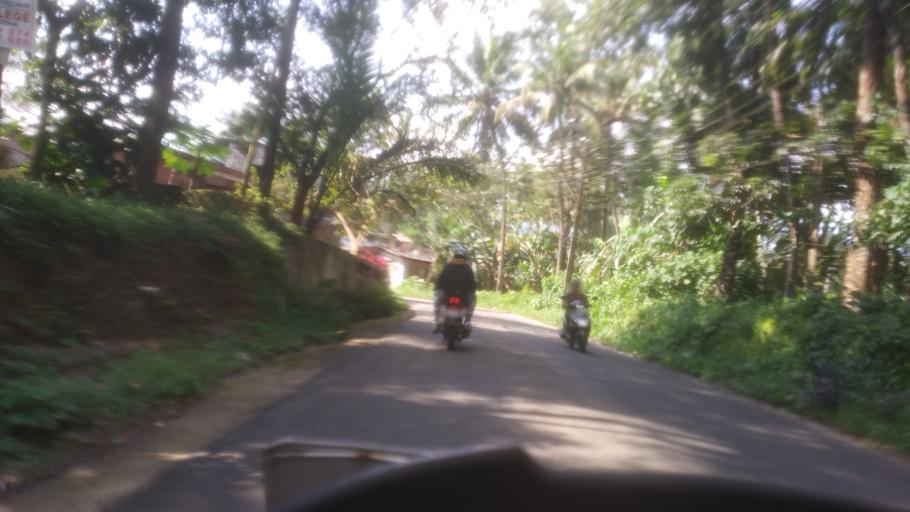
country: IN
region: Kerala
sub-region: Ernakulam
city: Kotamangalam
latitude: 10.0074
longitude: 76.7144
